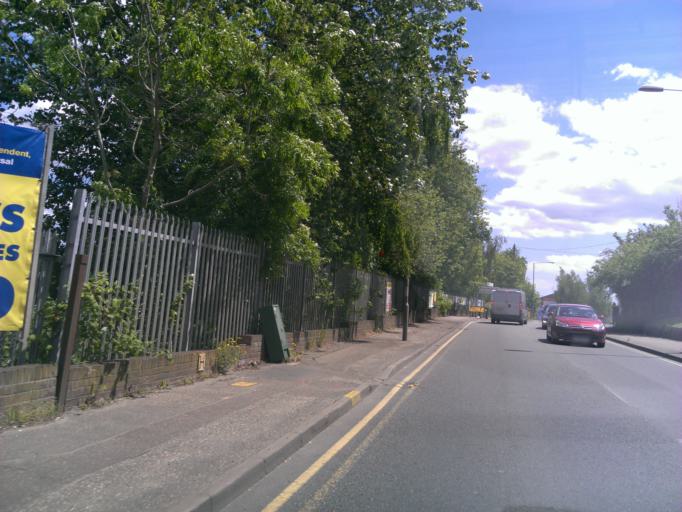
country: GB
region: England
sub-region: Essex
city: Rowhedge
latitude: 51.8773
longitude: 0.9317
